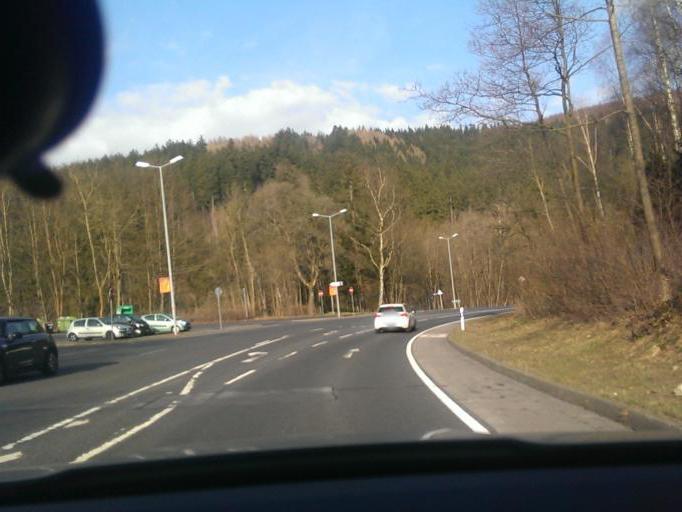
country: DE
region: Thuringia
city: Suhl
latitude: 50.5957
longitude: 10.7187
